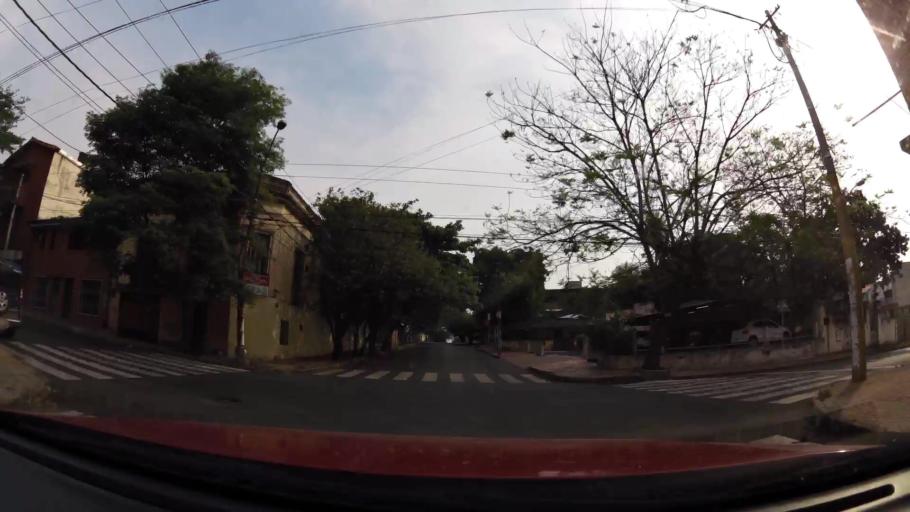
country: PY
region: Asuncion
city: Asuncion
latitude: -25.2927
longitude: -57.6176
